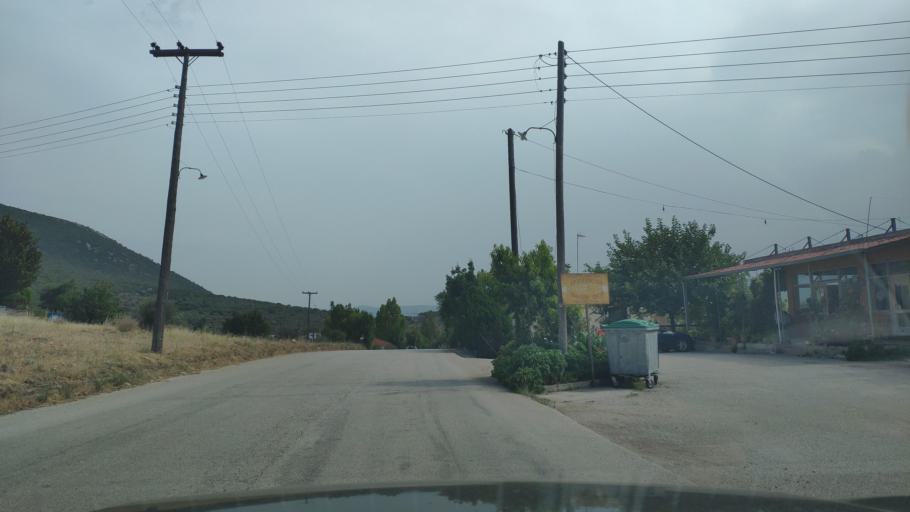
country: GR
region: Peloponnese
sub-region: Nomos Argolidos
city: Palaia Epidavros
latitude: 37.5938
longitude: 23.1582
